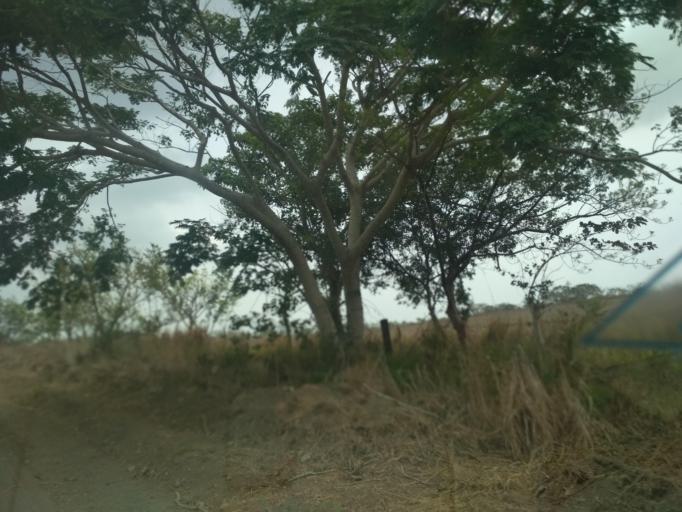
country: MX
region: Veracruz
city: Paso del Toro
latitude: 19.0129
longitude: -96.1337
